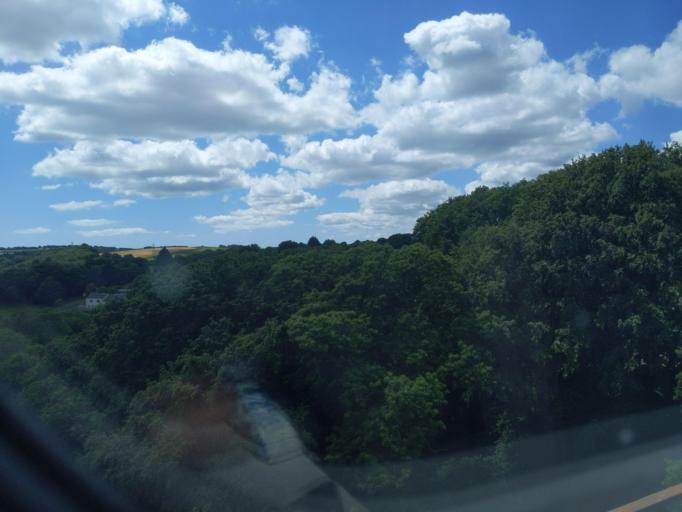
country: GB
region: England
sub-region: Cornwall
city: Liskeard
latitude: 50.4253
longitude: -4.4064
